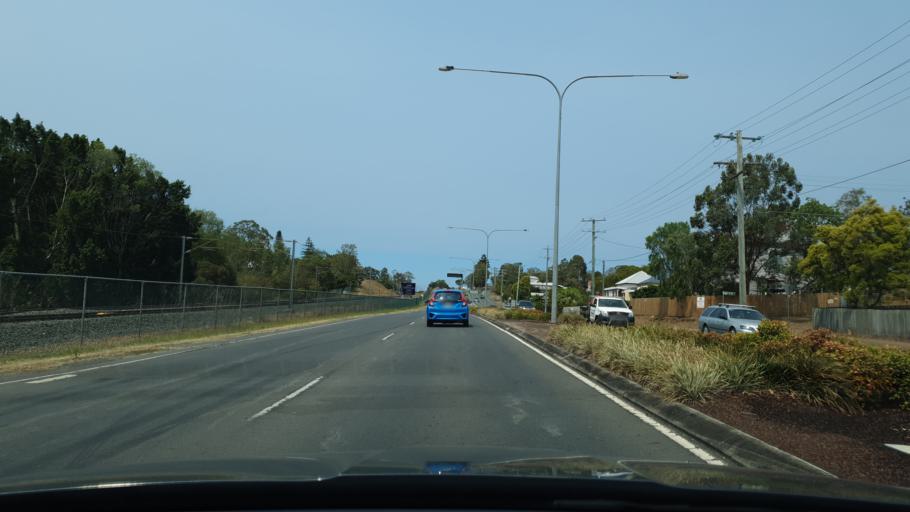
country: AU
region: Queensland
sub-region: Ipswich
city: Bundamba
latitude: -27.6069
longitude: 152.8145
